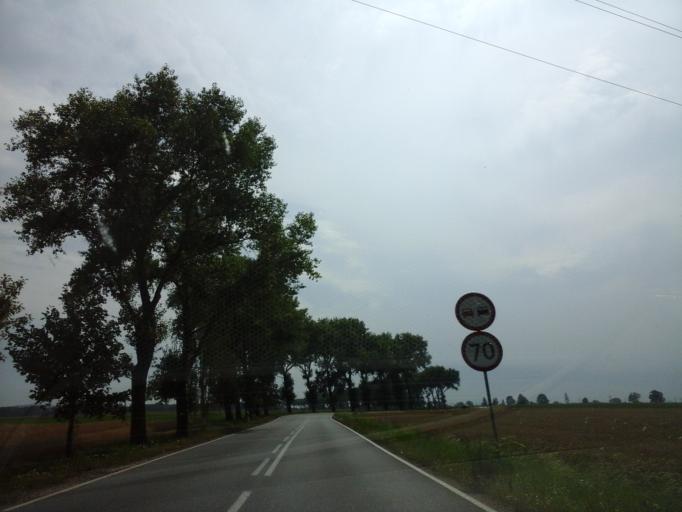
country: PL
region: Lower Silesian Voivodeship
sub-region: Powiat strzelinski
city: Strzelin
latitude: 50.8204
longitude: 17.0601
